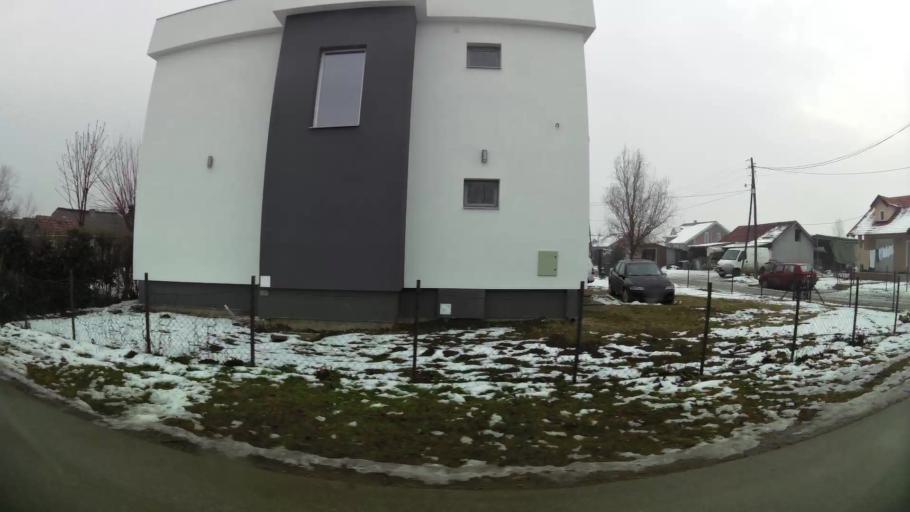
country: MK
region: Petrovec
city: Petrovec
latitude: 41.9353
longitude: 21.6090
